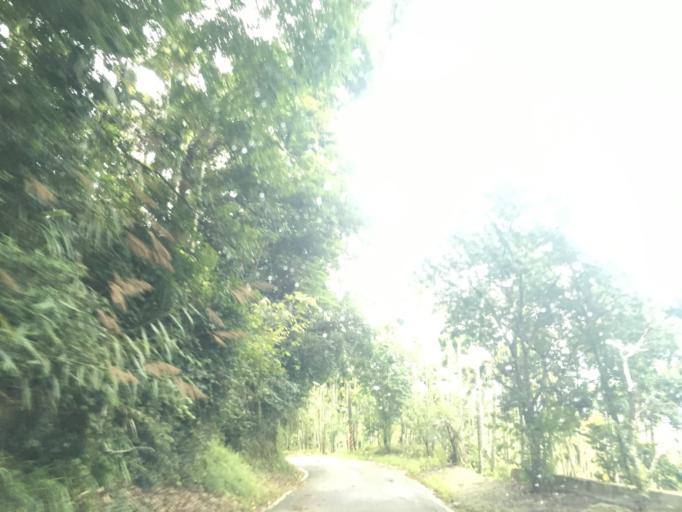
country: TW
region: Taiwan
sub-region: Yunlin
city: Douliu
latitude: 23.5623
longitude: 120.6210
